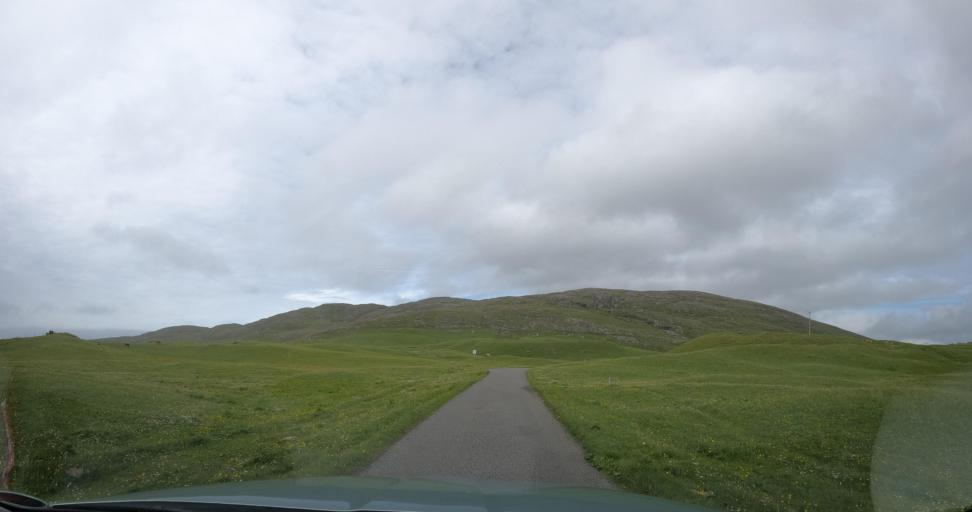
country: GB
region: Scotland
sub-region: Eilean Siar
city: Barra
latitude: 56.9237
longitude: -7.5385
